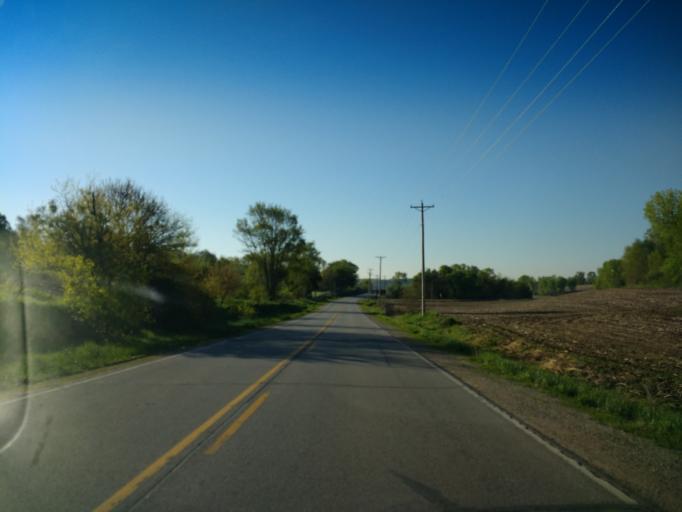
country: US
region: Iowa
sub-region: Harrison County
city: Missouri Valley
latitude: 41.4176
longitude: -95.8474
